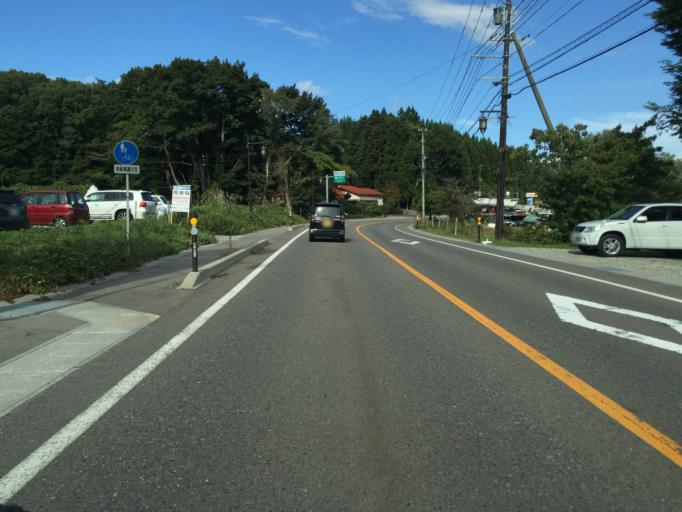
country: JP
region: Fukushima
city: Inawashiro
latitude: 37.5237
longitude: 140.0472
